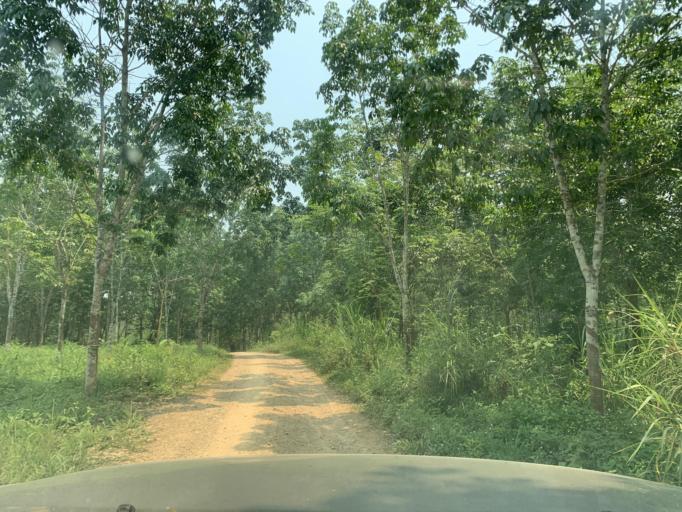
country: LA
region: Louangphabang
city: Xiang Ngeun
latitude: 19.8275
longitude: 102.2174
